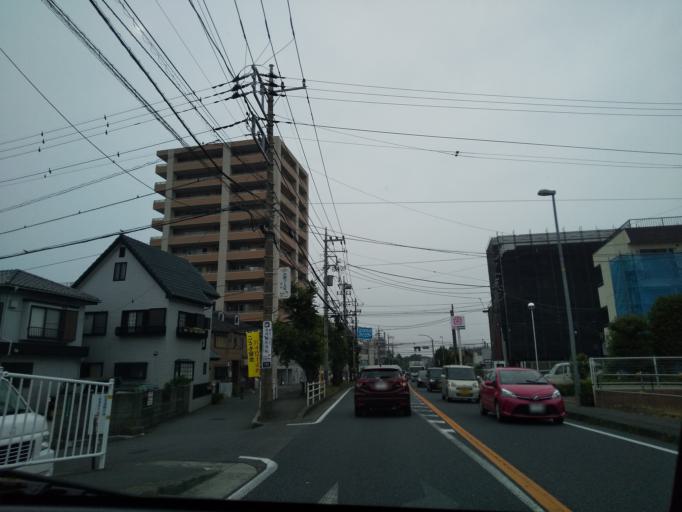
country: JP
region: Kanagawa
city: Zama
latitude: 35.5077
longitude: 139.4153
